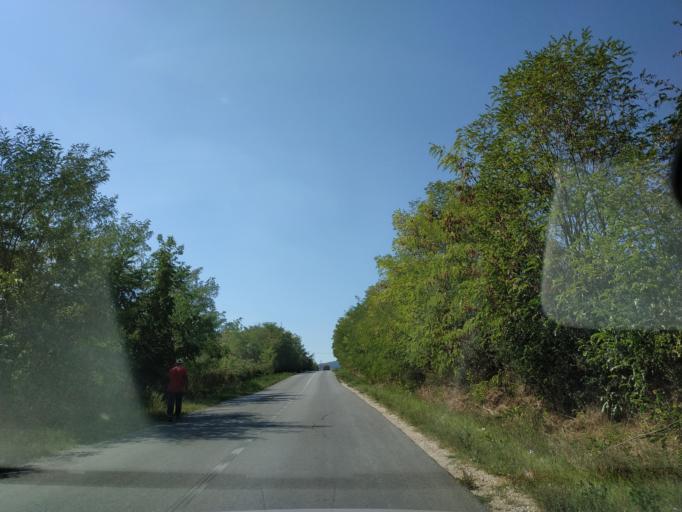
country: RS
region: Central Serbia
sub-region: Sumadijski Okrug
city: Arangelovac
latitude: 44.2980
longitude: 20.5843
